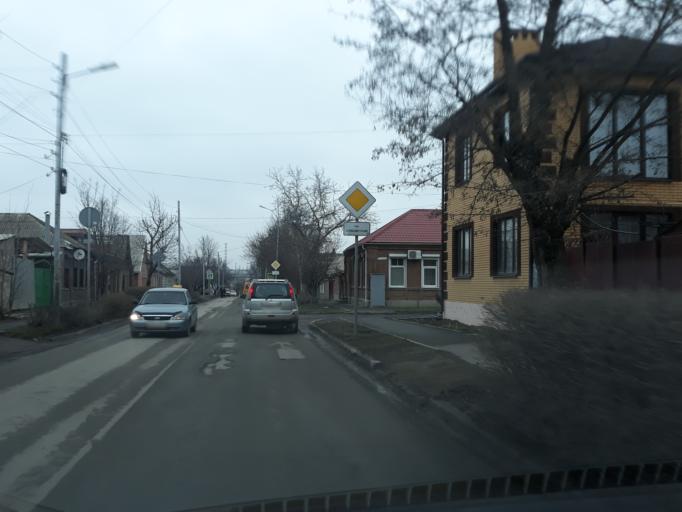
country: RU
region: Rostov
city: Taganrog
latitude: 47.2284
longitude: 38.9243
